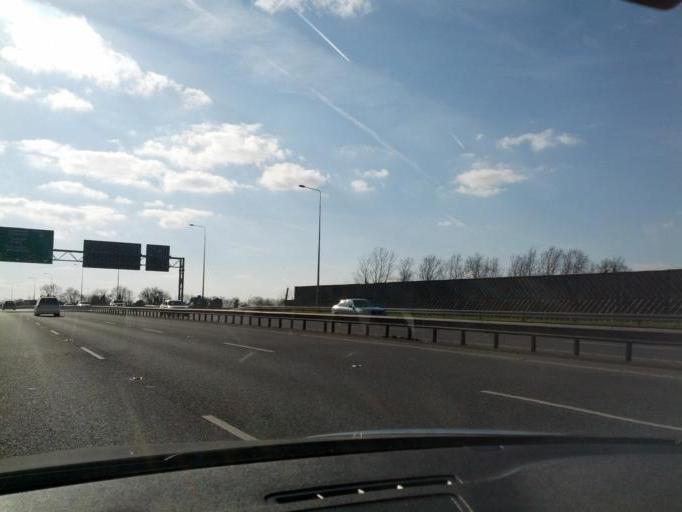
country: IE
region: Leinster
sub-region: Kildare
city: Kill
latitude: 53.2496
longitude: -6.5915
